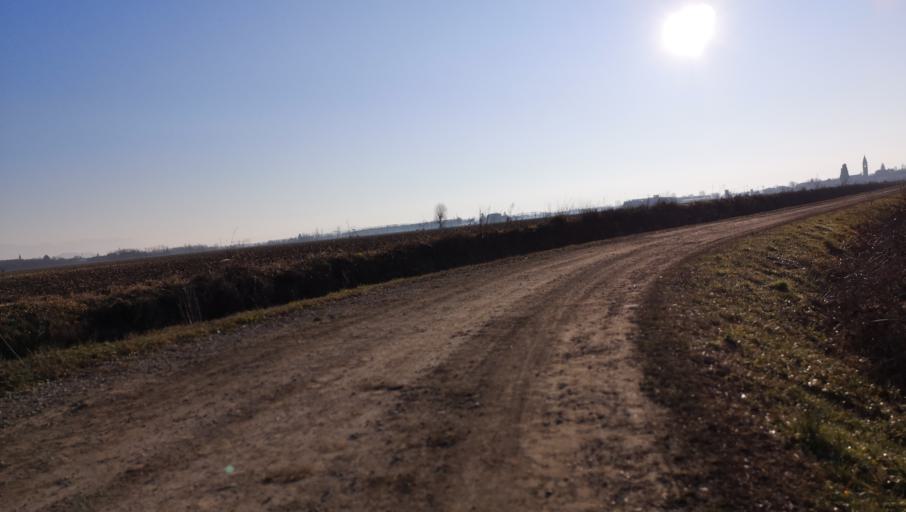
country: IT
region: Friuli Venezia Giulia
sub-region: Provincia di Udine
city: Lauzacco
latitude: 45.9733
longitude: 13.2922
